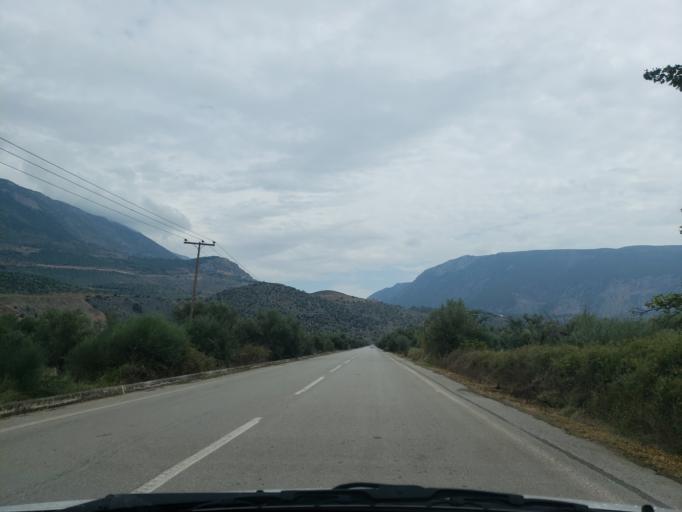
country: GR
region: Central Greece
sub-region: Nomos Fokidos
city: Kirra
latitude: 38.4794
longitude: 22.4419
